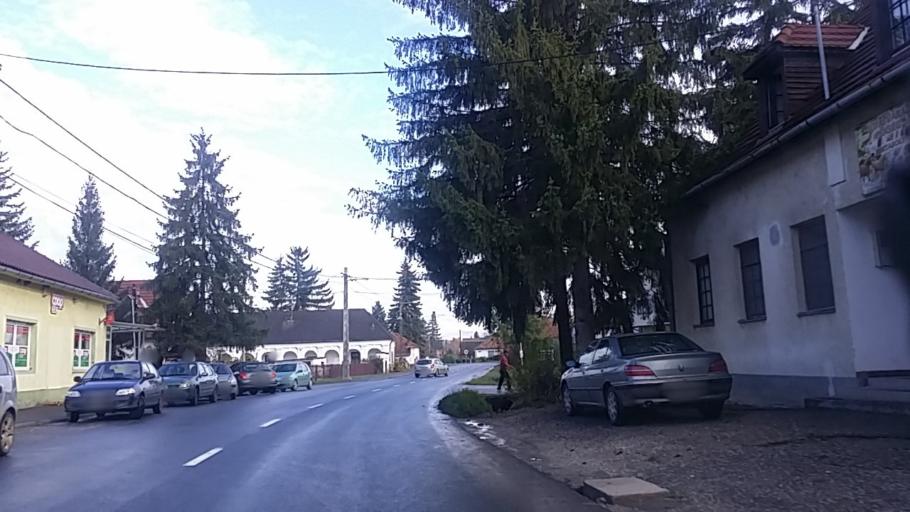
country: HU
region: Heves
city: Szilvasvarad
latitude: 48.1077
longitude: 20.3877
